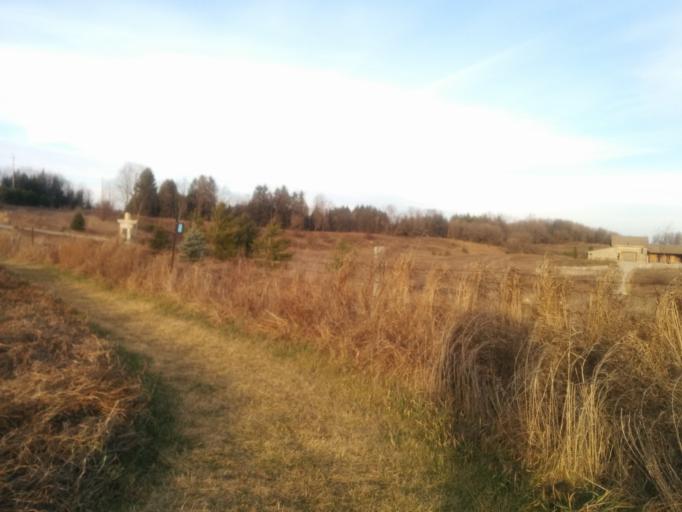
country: CA
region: Ontario
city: Orangeville
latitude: 43.9604
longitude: -79.9796
